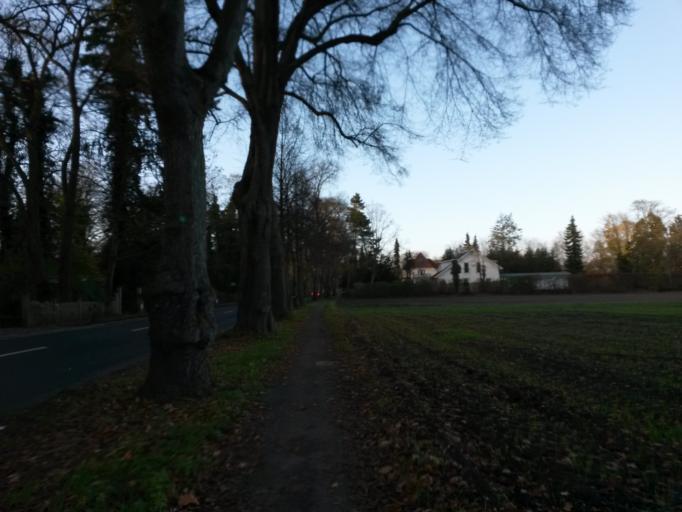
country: DE
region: Lower Saxony
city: Lilienthal
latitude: 53.0856
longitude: 8.9324
